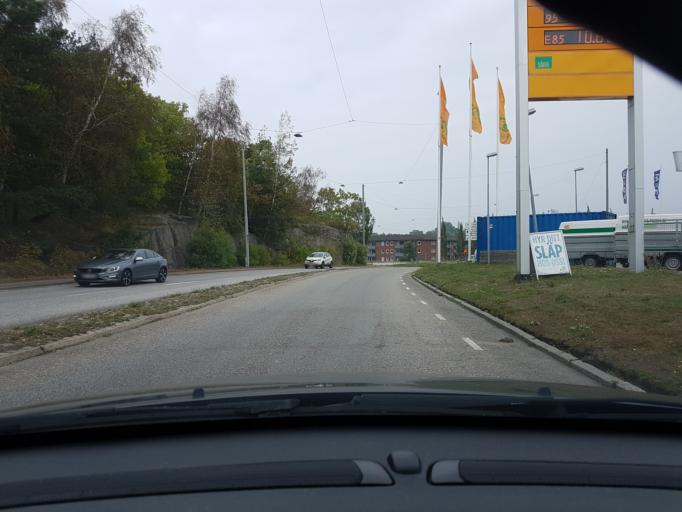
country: SE
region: Vaestra Goetaland
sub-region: Goteborg
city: Majorna
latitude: 57.6478
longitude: 11.8909
